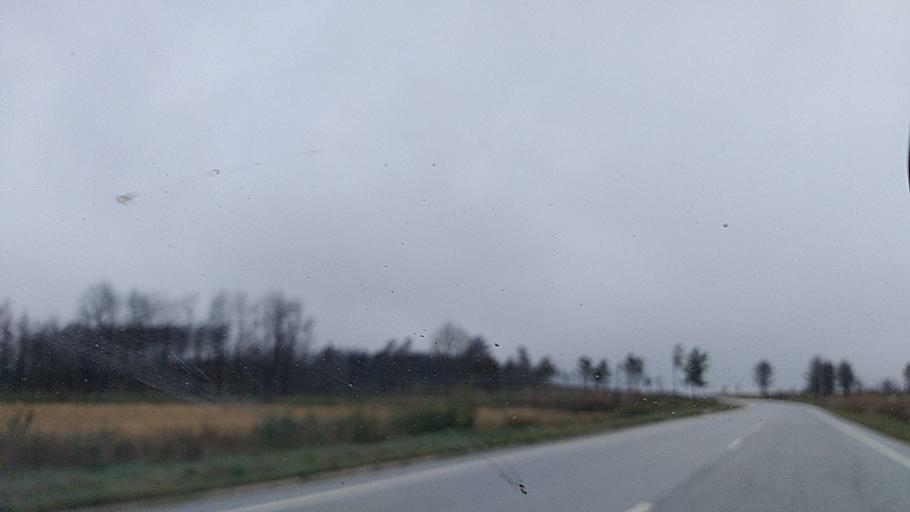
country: PT
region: Guarda
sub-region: Fornos de Algodres
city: Fornos de Algodres
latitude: 40.6987
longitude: -7.4750
